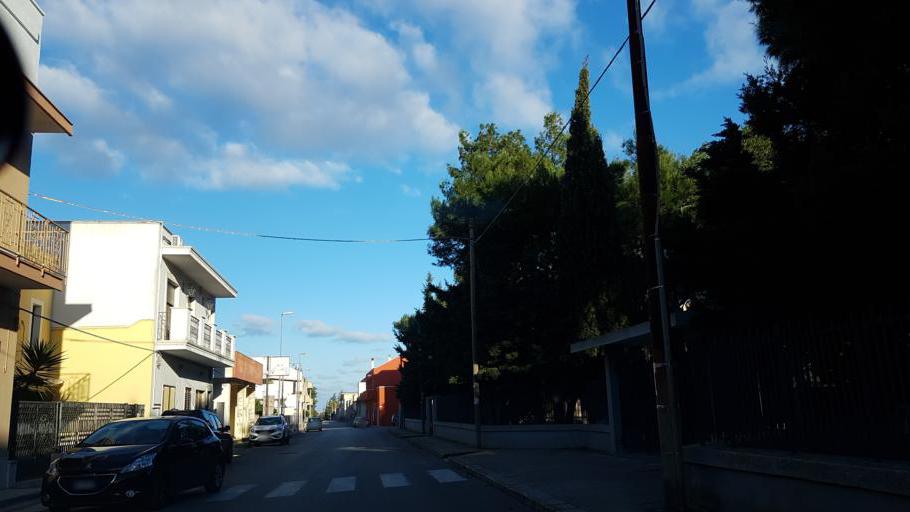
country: IT
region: Apulia
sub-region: Provincia di Lecce
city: Squinzano
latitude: 40.4418
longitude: 18.0366
